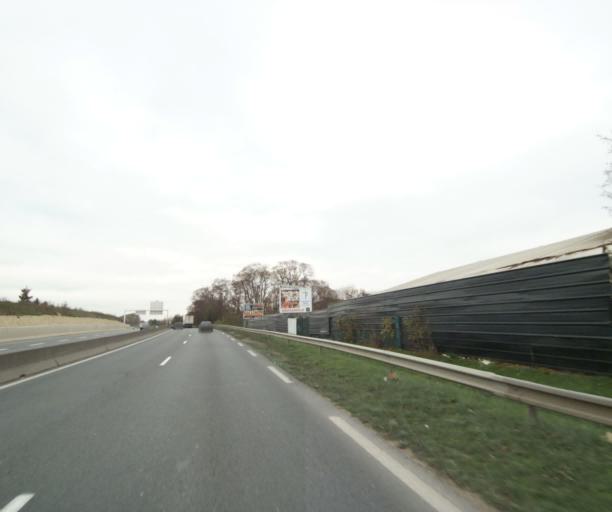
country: FR
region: Ile-de-France
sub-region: Departement du Val-d'Oise
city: Le Thillay
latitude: 49.0025
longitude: 2.4872
